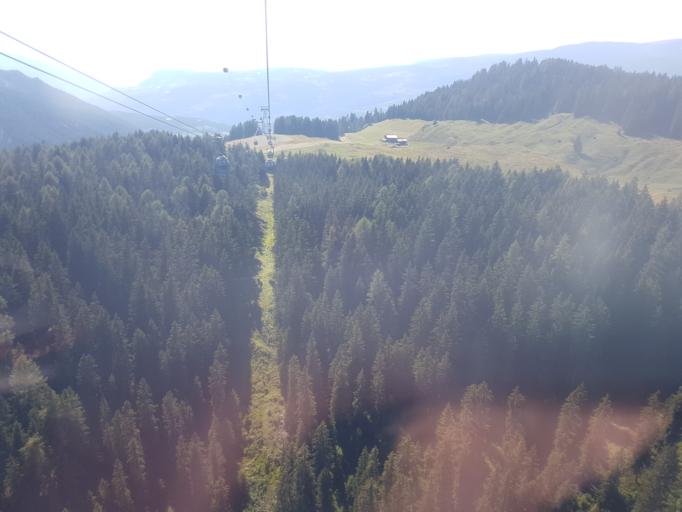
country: IT
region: Trentino-Alto Adige
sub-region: Bolzano
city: Siusi
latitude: 46.5417
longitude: 11.6035
